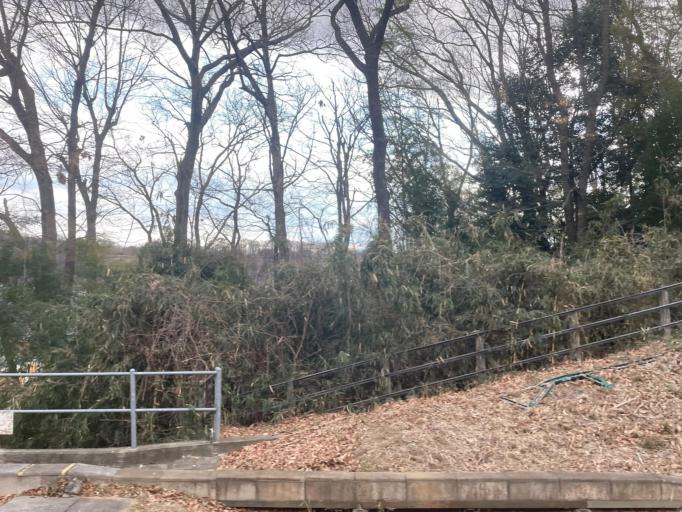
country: JP
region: Tokyo
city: Hachioji
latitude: 35.6450
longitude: 139.3346
